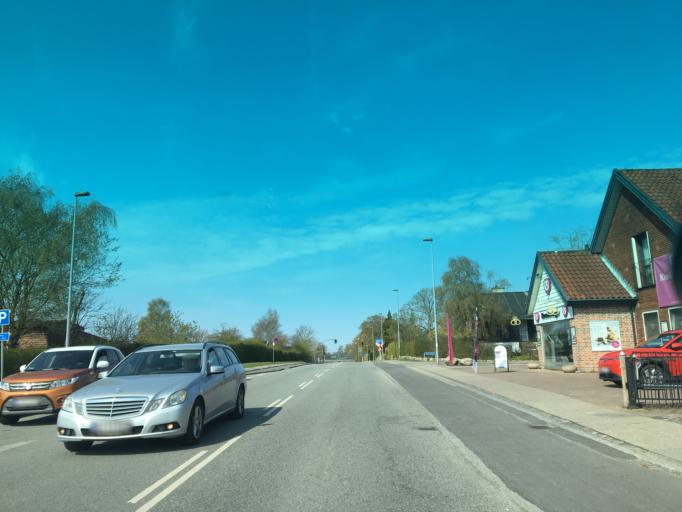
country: DK
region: Capital Region
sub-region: Herlev Kommune
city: Herlev
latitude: 55.7460
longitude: 12.4570
